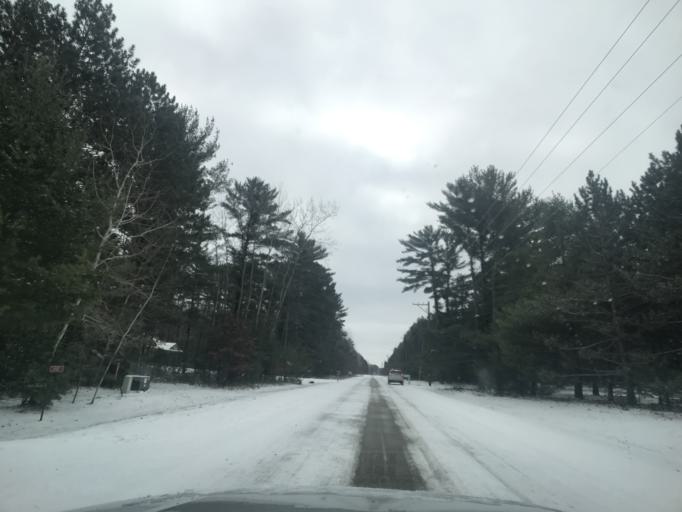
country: US
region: Wisconsin
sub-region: Brown County
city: Suamico
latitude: 44.6986
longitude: -88.1009
